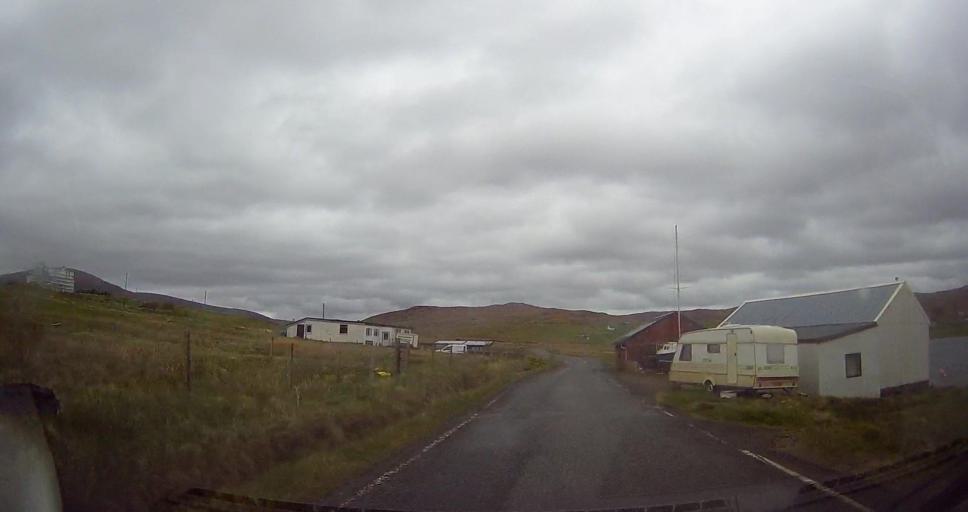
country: GB
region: Scotland
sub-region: Shetland Islands
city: Lerwick
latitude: 60.4896
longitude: -1.4650
